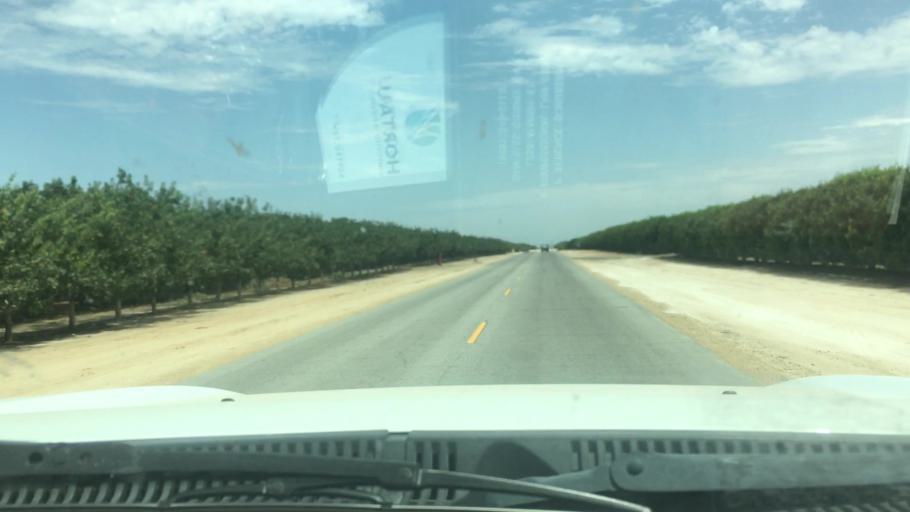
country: US
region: California
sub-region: Kern County
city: McFarland
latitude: 35.5772
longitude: -119.1511
